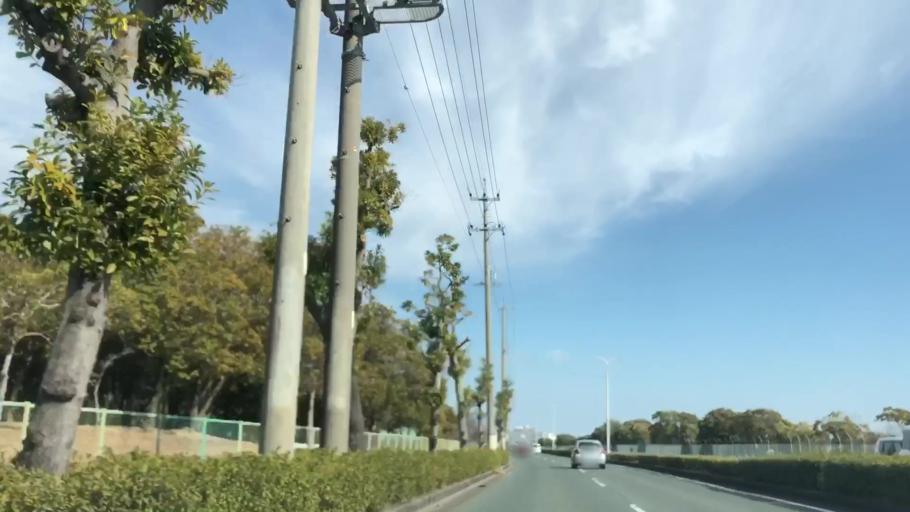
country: JP
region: Shizuoka
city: Hamamatsu
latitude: 34.7533
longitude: 137.7070
